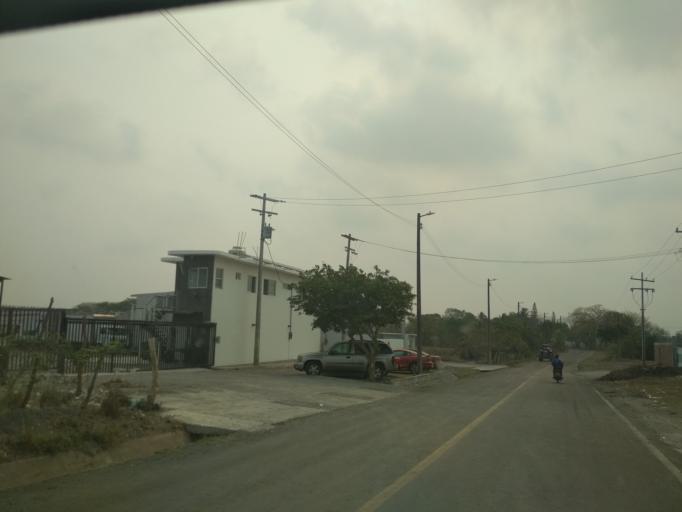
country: MX
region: Veracruz
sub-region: Veracruz
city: Delfino Victoria (Santa Fe)
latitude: 19.2101
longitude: -96.2516
